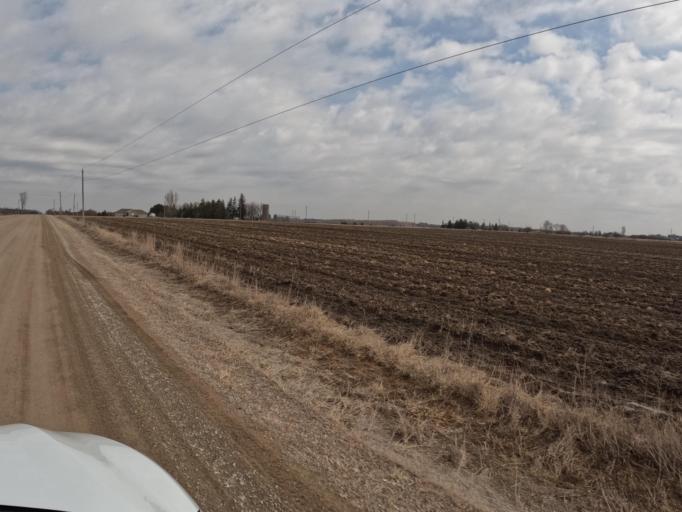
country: CA
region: Ontario
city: Orangeville
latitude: 43.9188
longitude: -80.2175
